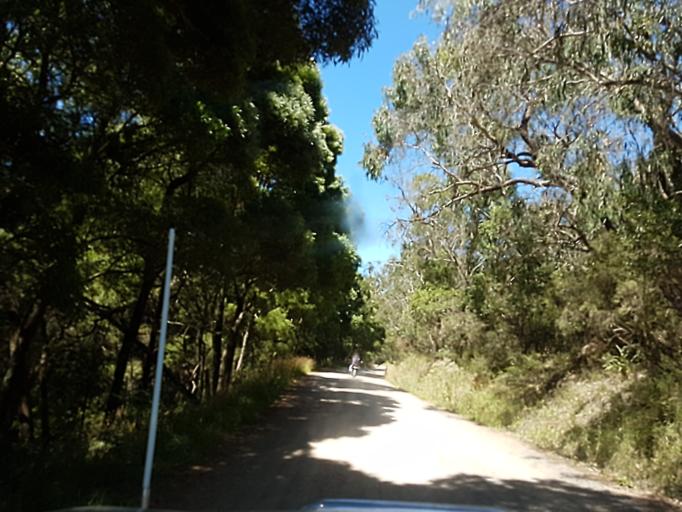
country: AU
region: Victoria
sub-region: Colac-Otway
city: Apollo Bay
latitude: -38.6354
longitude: 143.2974
